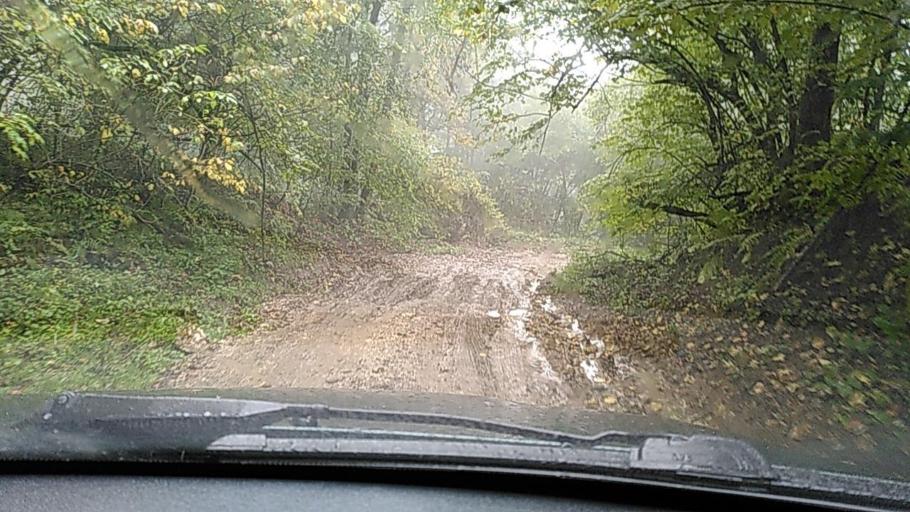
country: RU
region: Kabardino-Balkariya
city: Belaya Rechka
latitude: 43.3603
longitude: 43.4123
